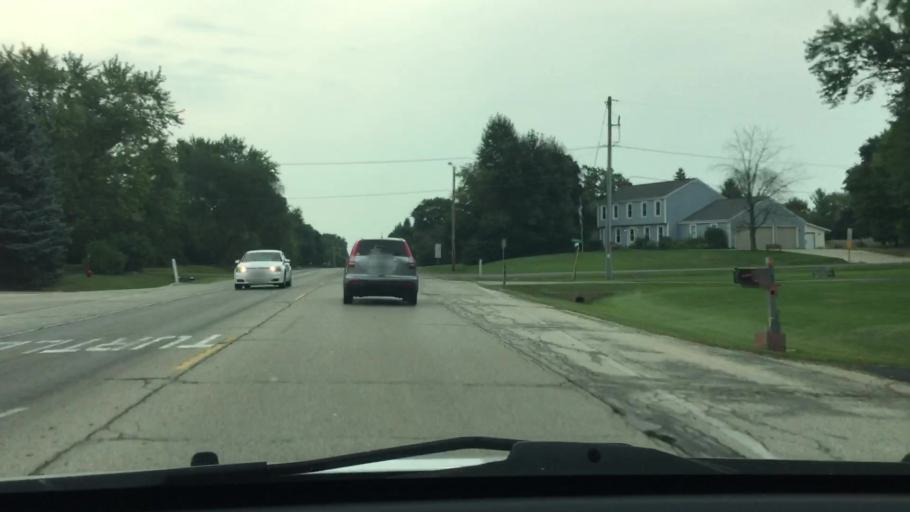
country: US
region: Wisconsin
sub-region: Waukesha County
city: New Berlin
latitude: 42.9955
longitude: -88.0975
